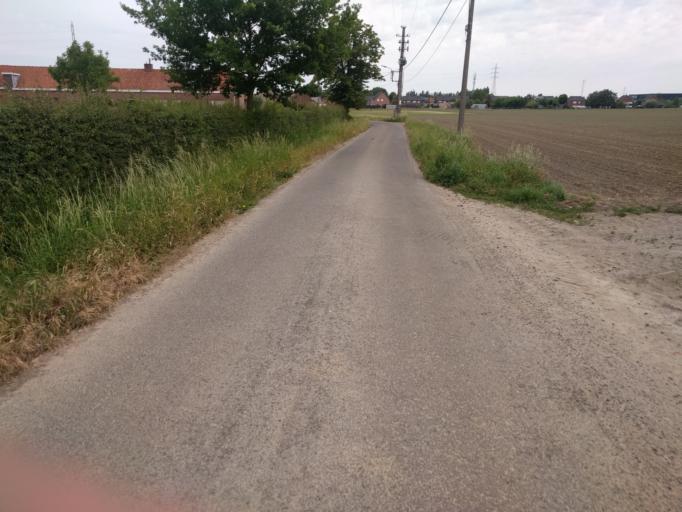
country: BE
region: Flanders
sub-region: Provincie West-Vlaanderen
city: Wevelgem
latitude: 50.8340
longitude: 3.1740
